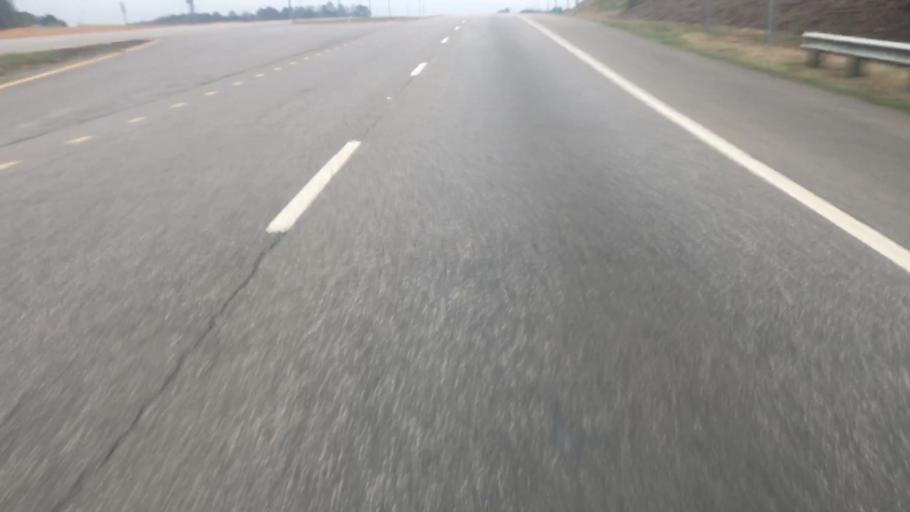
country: US
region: Alabama
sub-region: Jefferson County
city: Graysville
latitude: 33.6513
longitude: -86.9748
